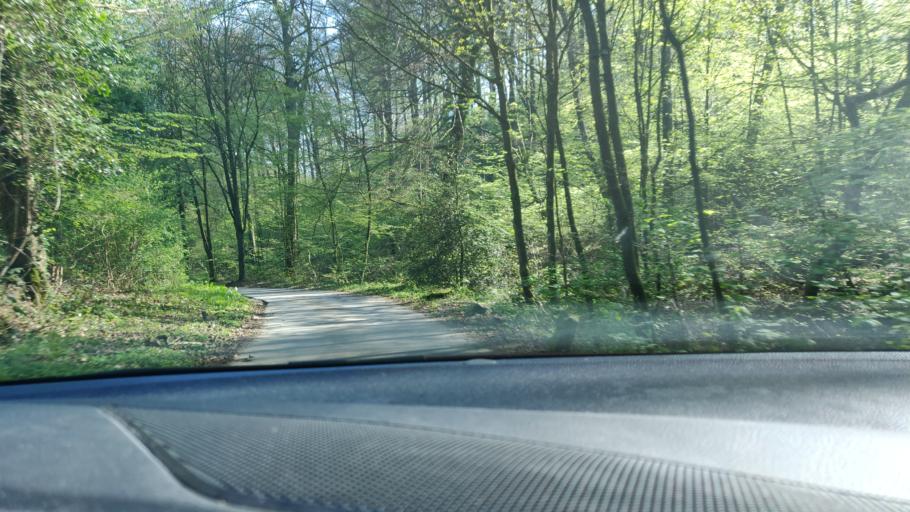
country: DE
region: North Rhine-Westphalia
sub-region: Regierungsbezirk Dusseldorf
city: Velbert
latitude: 51.3353
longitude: 7.0641
